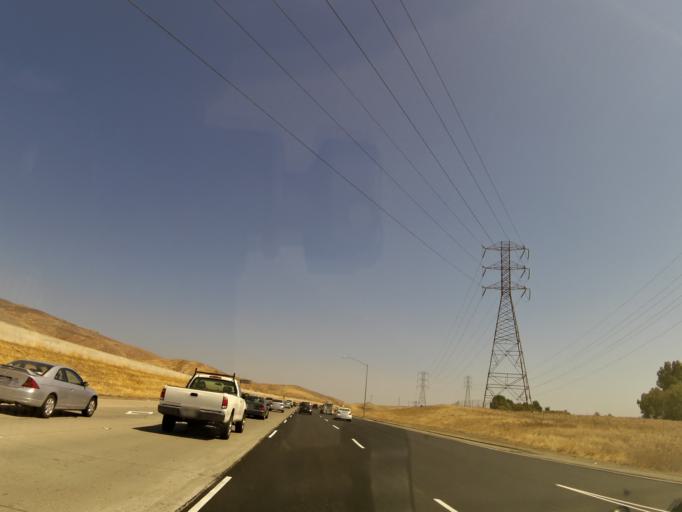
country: US
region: California
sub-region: Santa Clara County
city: Morgan Hill
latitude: 37.1879
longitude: -121.6895
